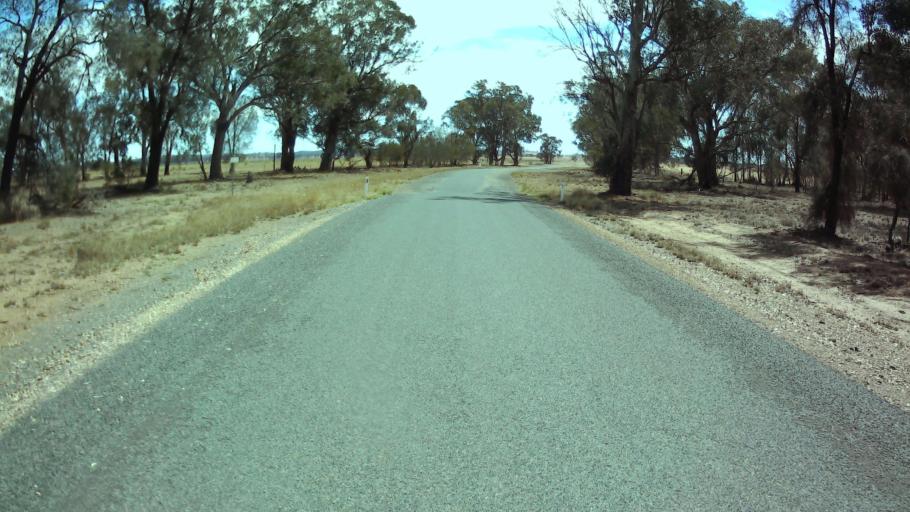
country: AU
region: New South Wales
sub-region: Weddin
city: Grenfell
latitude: -33.6424
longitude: 148.1898
